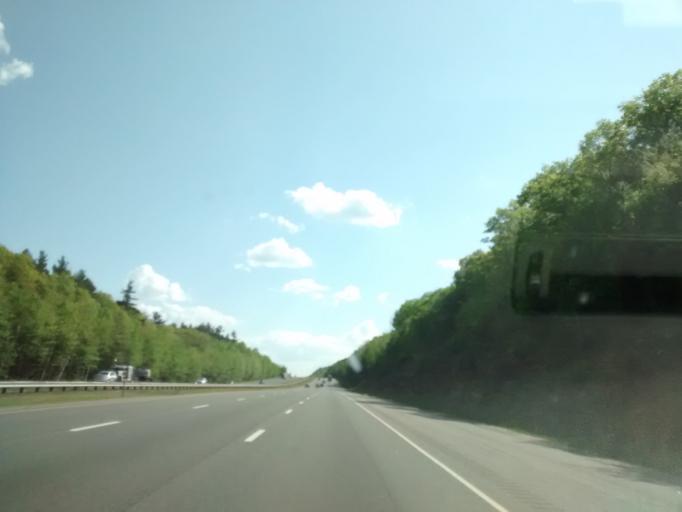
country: US
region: Massachusetts
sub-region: Hampden County
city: Holland
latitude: 42.0144
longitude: -72.1565
